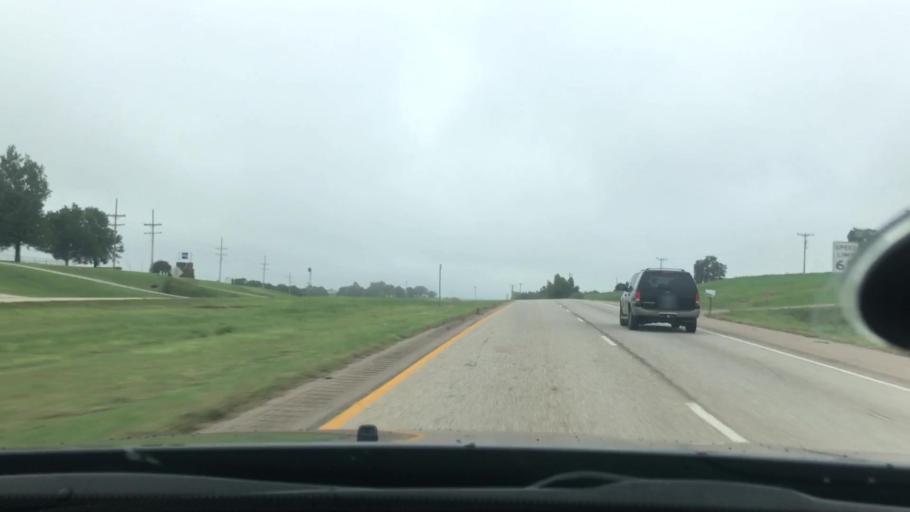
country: US
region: Oklahoma
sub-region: Seminole County
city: Seminole
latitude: 35.3065
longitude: -96.6707
